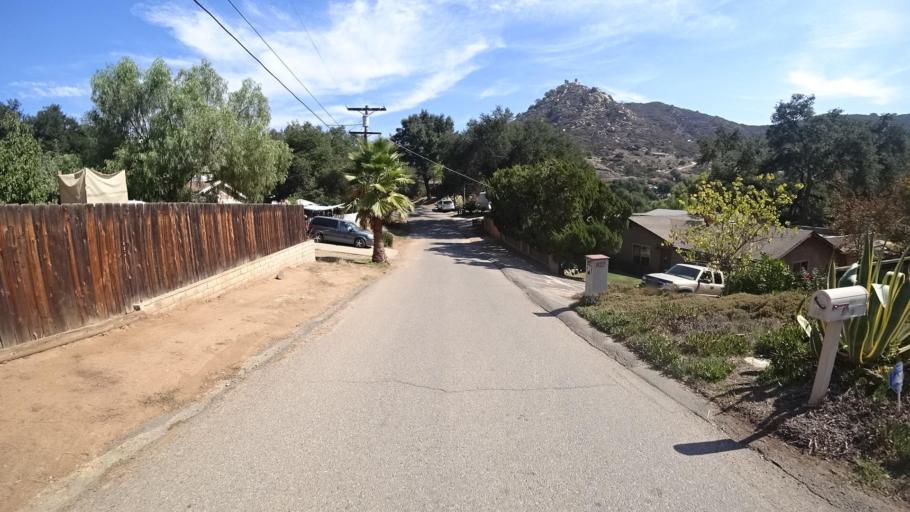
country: US
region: California
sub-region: San Diego County
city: Harbison Canyon
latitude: 32.8160
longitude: -116.8358
